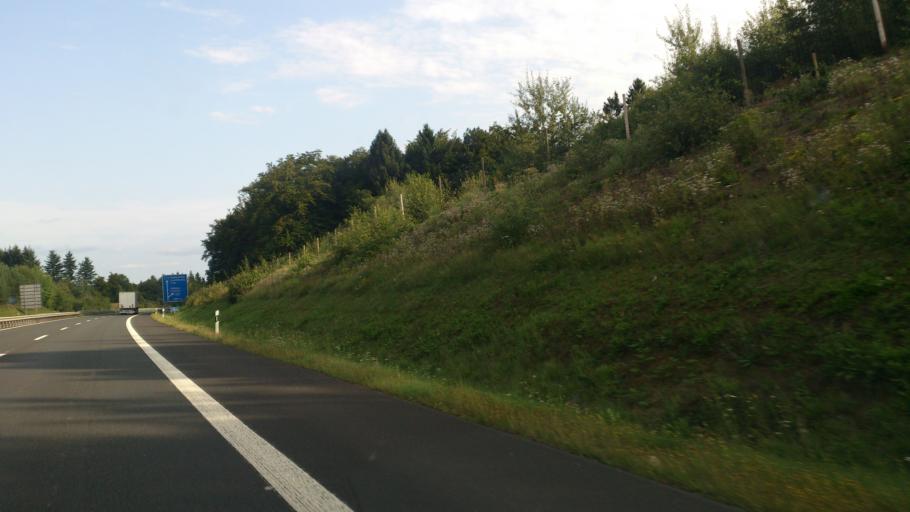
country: DE
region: Rheinland-Pfalz
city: Darscheid
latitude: 50.2050
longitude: 6.8855
